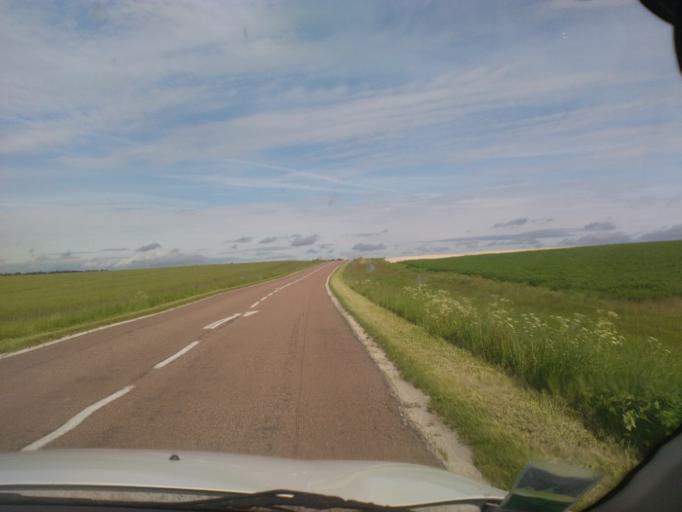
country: FR
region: Champagne-Ardenne
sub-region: Departement de l'Aube
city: Payns
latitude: 48.3745
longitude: 3.8857
